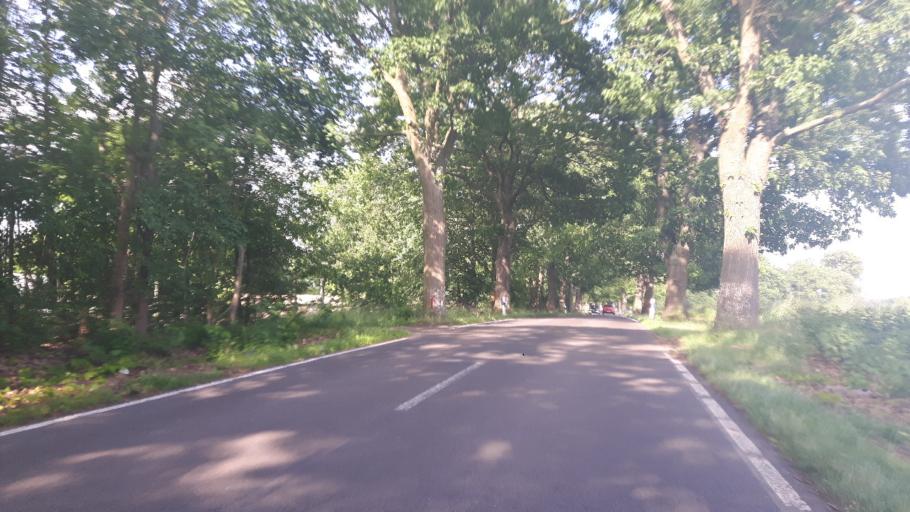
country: DE
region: Brandenburg
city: Melchow
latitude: 52.7459
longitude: 13.7310
